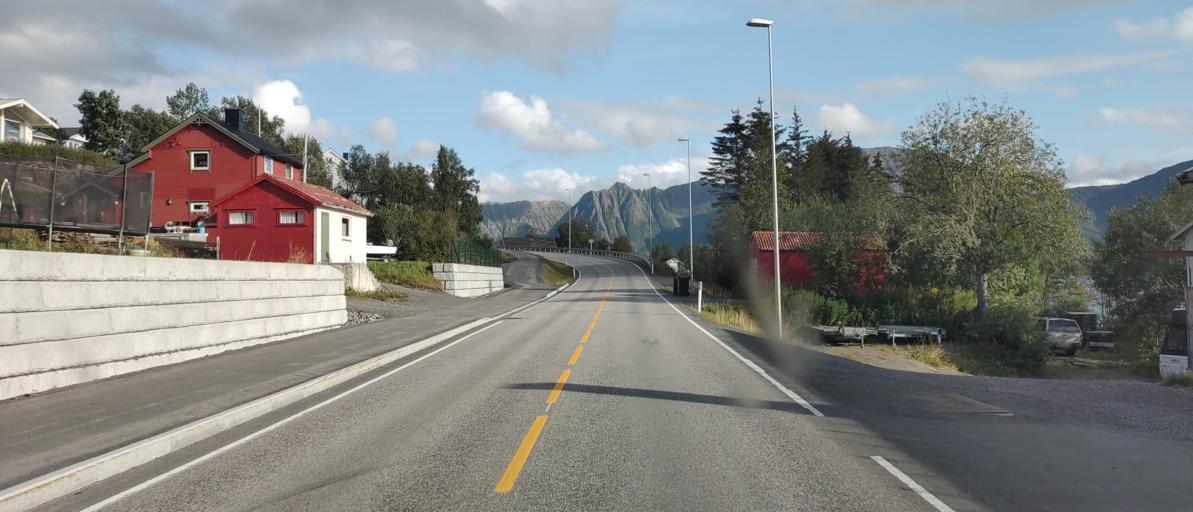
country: NO
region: Nordland
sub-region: Sortland
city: Sortland
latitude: 68.7524
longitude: 15.4736
